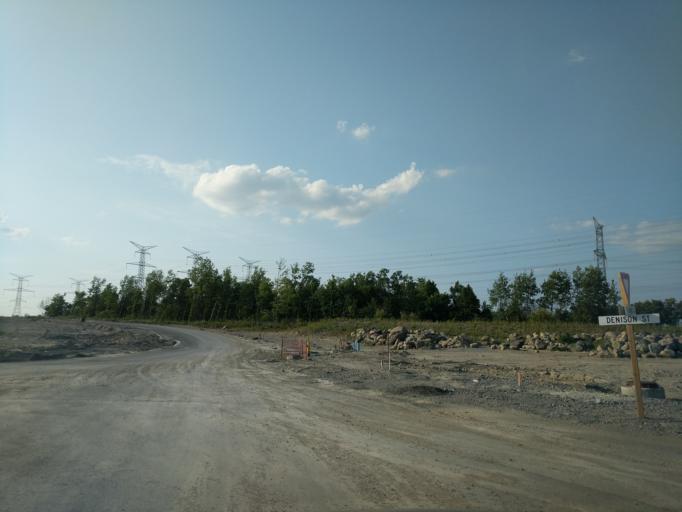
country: CA
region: Ontario
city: Markham
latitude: 43.8488
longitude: -79.2411
